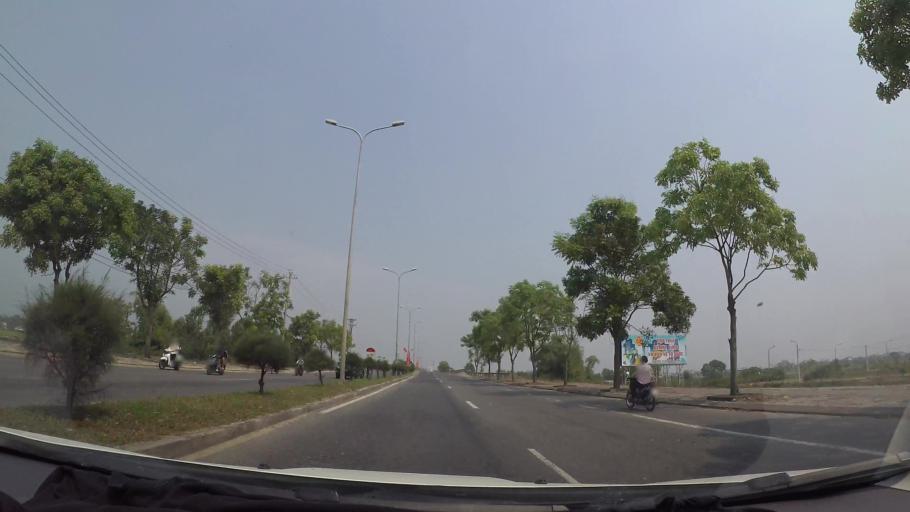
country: VN
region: Da Nang
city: Cam Le
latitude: 15.9711
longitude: 108.2091
